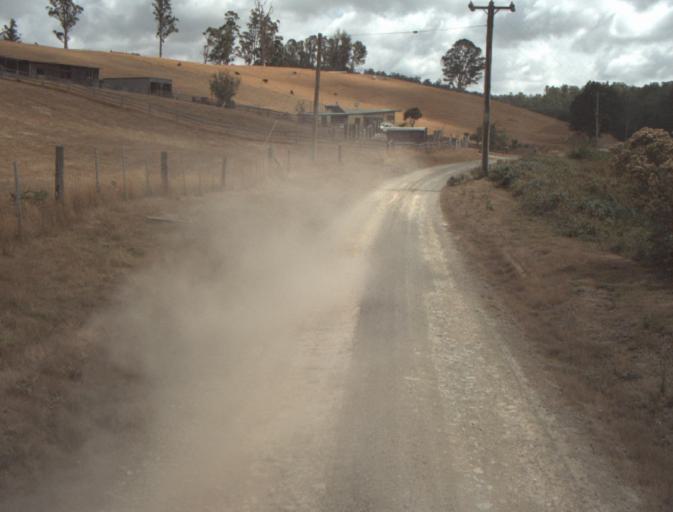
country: AU
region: Tasmania
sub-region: Dorset
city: Bridport
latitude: -41.1894
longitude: 147.2617
